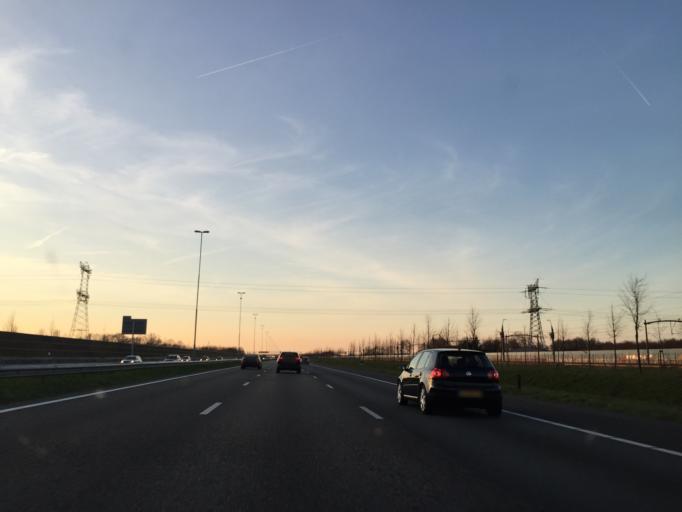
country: NL
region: North Brabant
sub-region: Gemeente Breda
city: Breda
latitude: 51.6170
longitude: 4.7125
